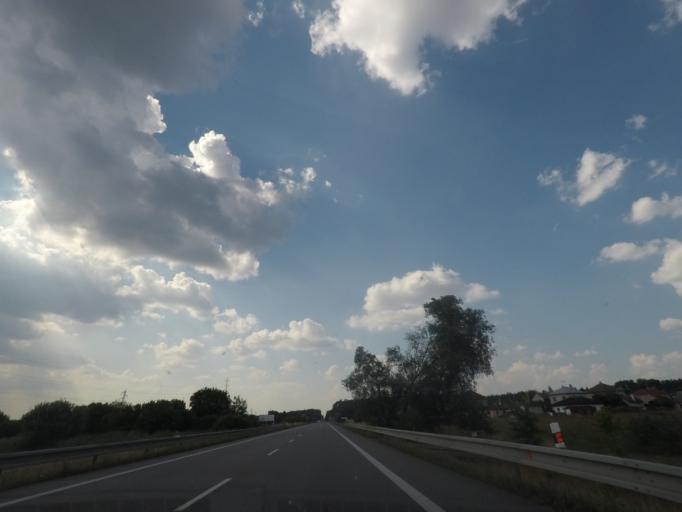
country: CZ
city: Albrechtice nad Orlici
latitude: 50.1704
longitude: 16.0404
